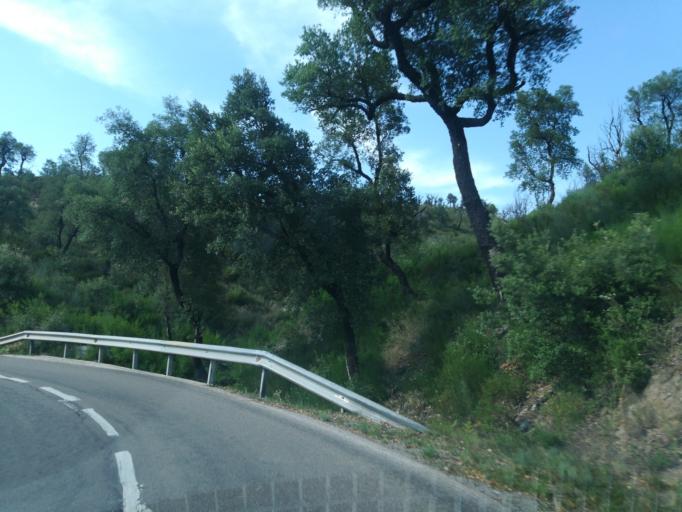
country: ES
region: Catalonia
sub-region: Provincia de Girona
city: Darnius
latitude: 42.3678
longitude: 2.8594
